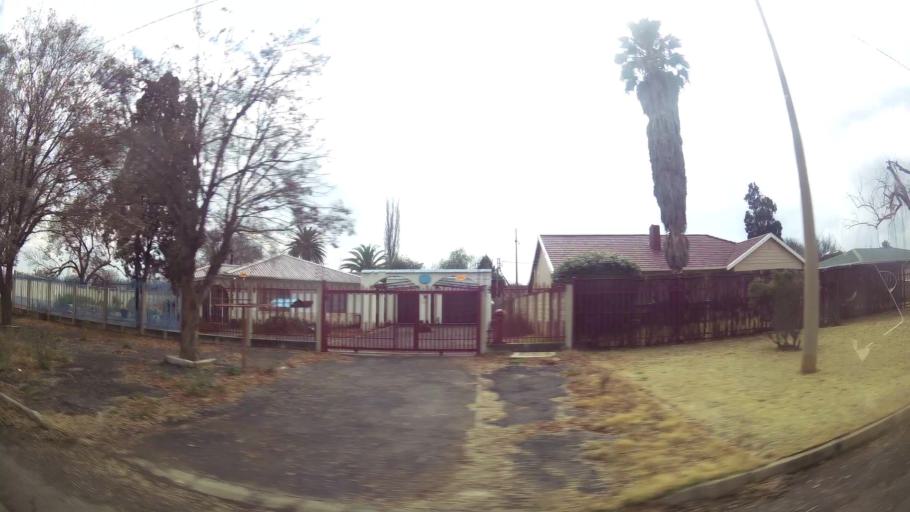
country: ZA
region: Gauteng
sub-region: Sedibeng District Municipality
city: Vereeniging
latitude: -26.6539
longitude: 27.9878
